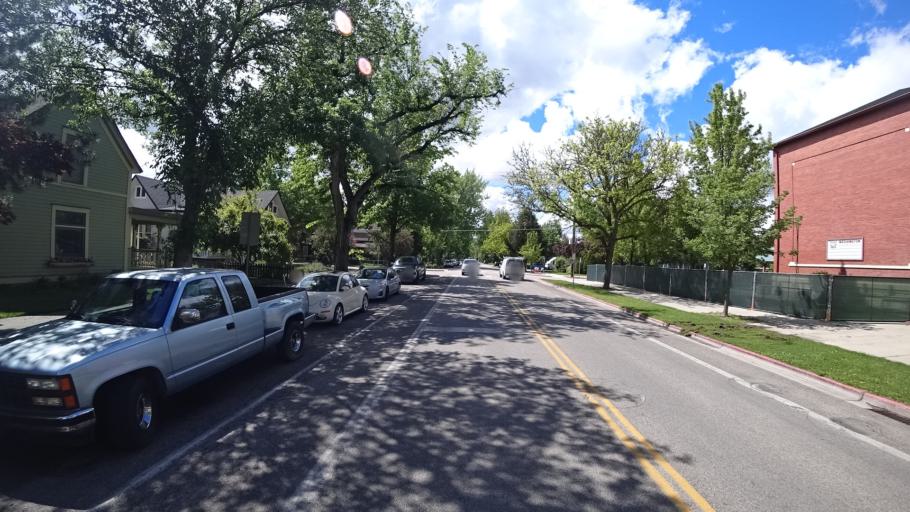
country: US
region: Idaho
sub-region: Ada County
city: Boise
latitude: 43.6323
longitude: -116.2058
